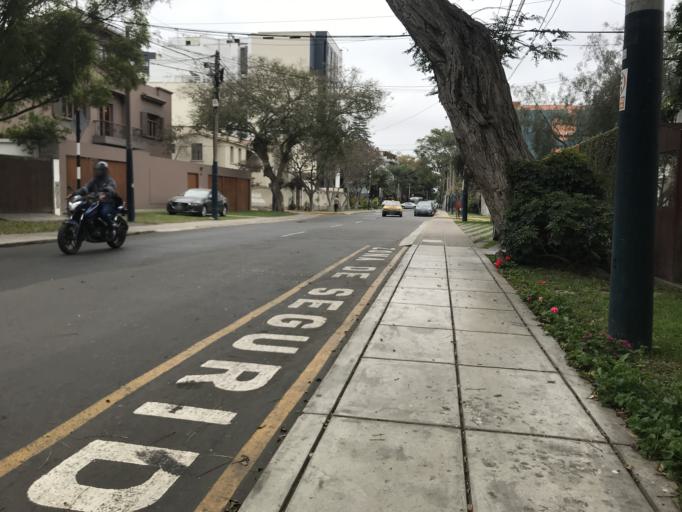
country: PE
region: Lima
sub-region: Lima
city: San Isidro
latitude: -12.0959
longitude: -77.0338
